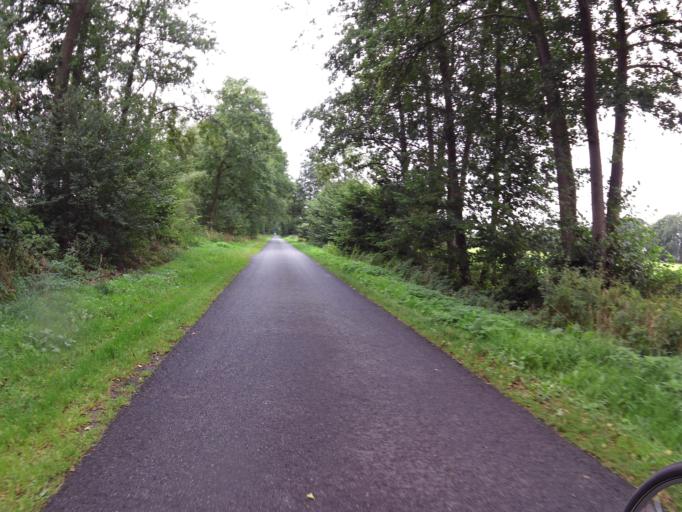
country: DE
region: Lower Saxony
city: Scheessel
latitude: 53.1623
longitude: 9.4615
